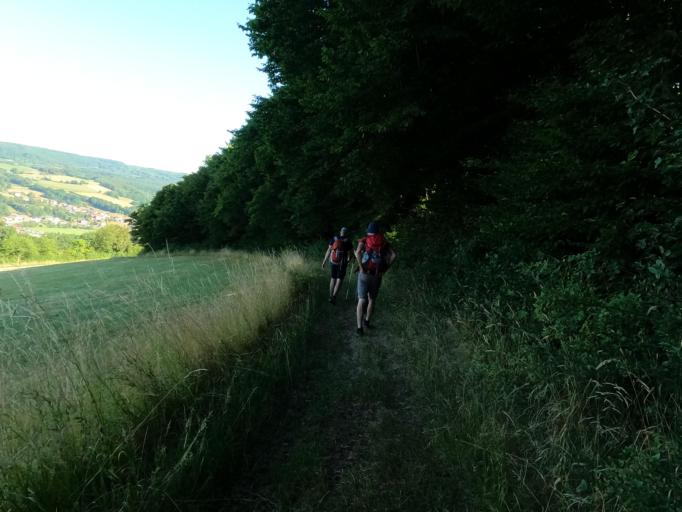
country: DE
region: Bavaria
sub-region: Regierungsbezirk Unterfranken
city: Zeitlofs
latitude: 50.3039
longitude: 9.6726
